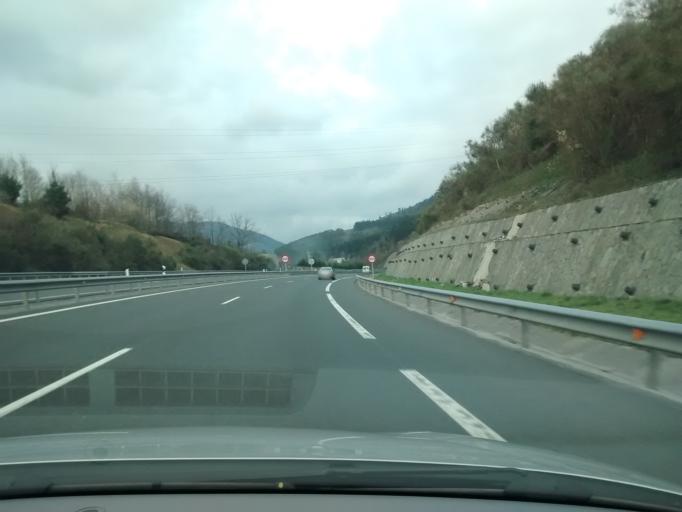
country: ES
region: Basque Country
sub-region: Bizkaia
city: Alonsotegi
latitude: 43.2194
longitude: -3.0233
